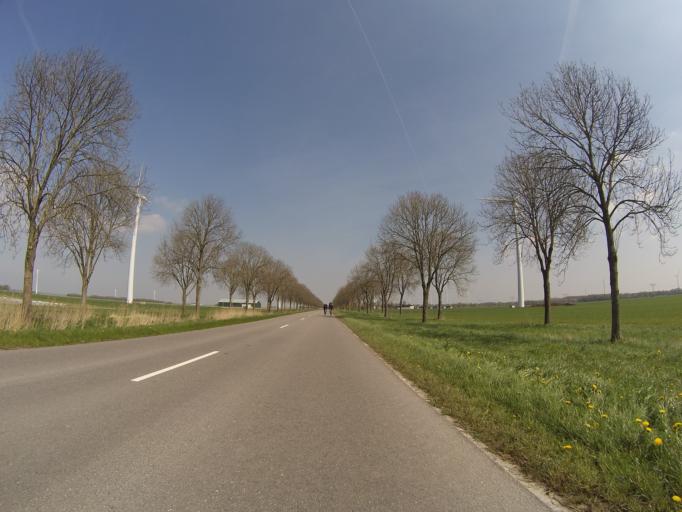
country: NL
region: Utrecht
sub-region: Gemeente Bunschoten
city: Spakenburg
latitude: 52.3291
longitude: 5.4039
